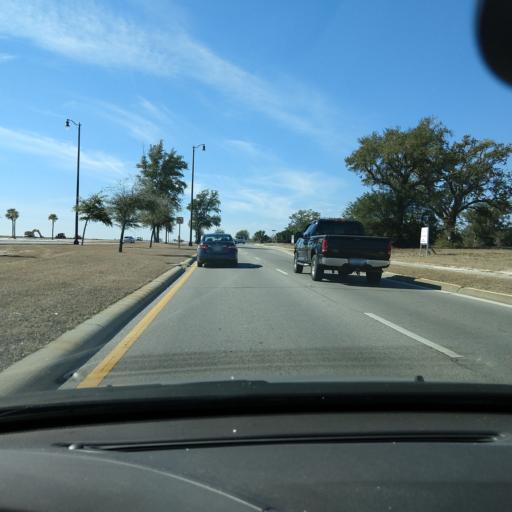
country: US
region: Mississippi
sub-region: Harrison County
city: Gulfport
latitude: 30.3576
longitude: -89.1141
